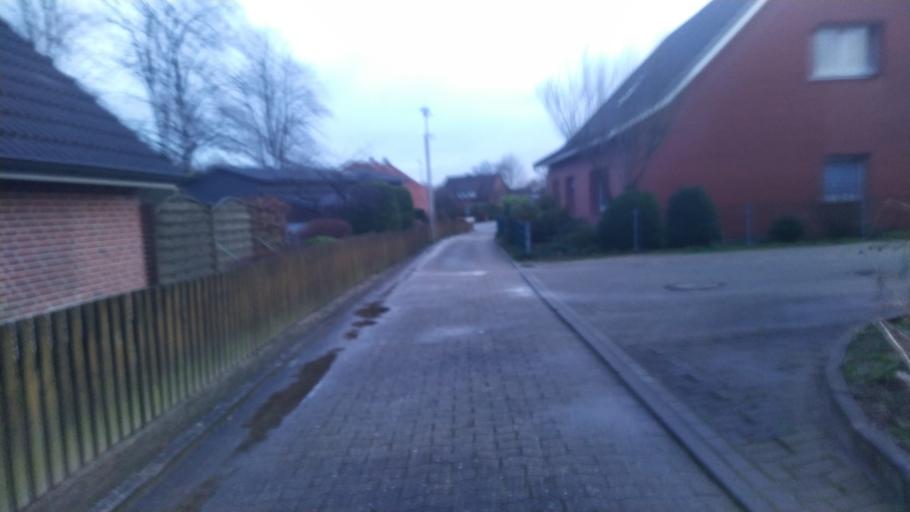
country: DE
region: Lower Saxony
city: Nottensdorf
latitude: 53.4765
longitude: 9.6120
